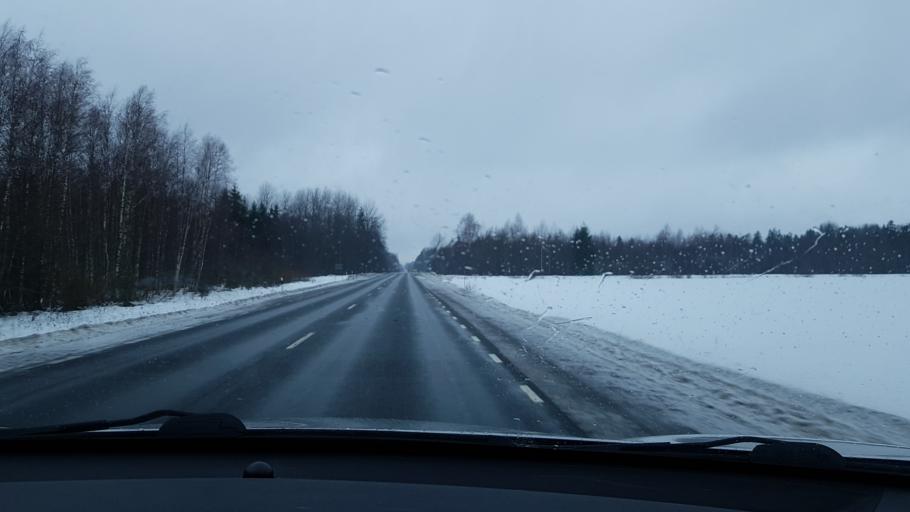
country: EE
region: Jaervamaa
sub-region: Tueri vald
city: Sarevere
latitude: 58.8044
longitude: 25.2189
